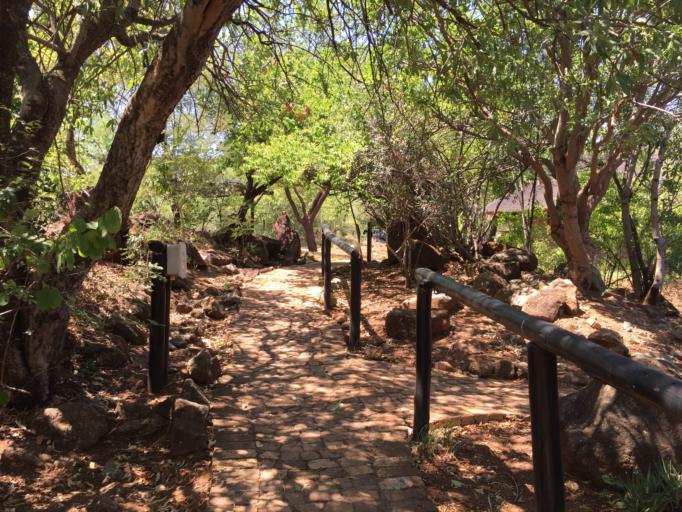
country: ZA
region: North-West
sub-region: Bojanala Platinum District Municipality
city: Mogwase
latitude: -25.3414
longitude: 27.0578
